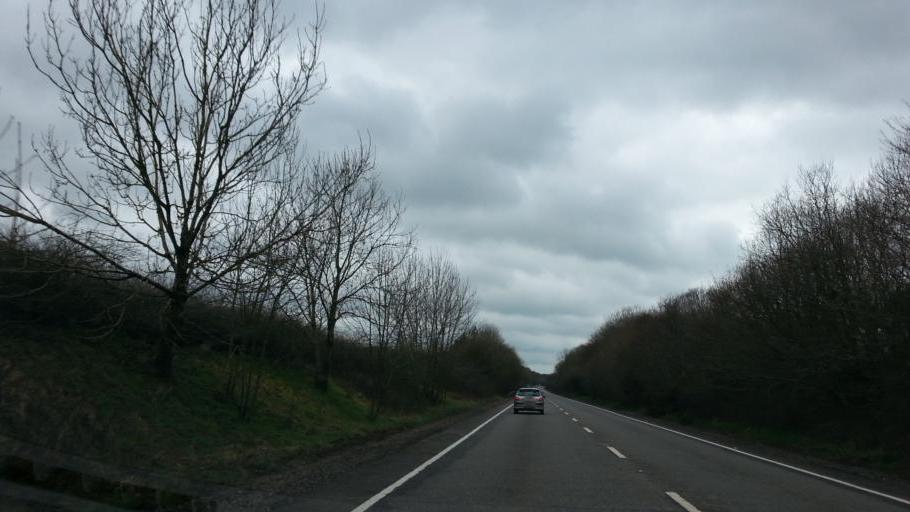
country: GB
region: England
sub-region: Devon
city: South Molton
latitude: 51.0490
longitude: -3.9049
